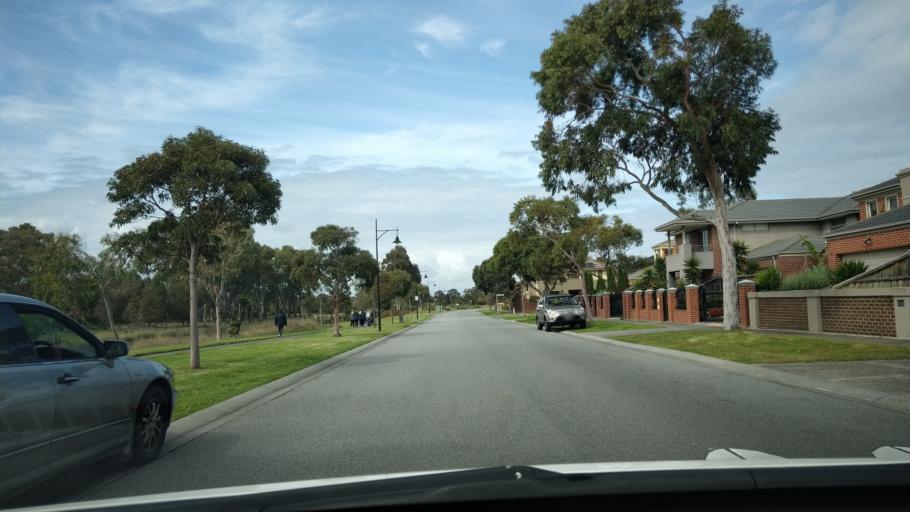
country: AU
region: Victoria
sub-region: Greater Dandenong
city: Keysborough
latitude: -37.9981
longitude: 145.1519
